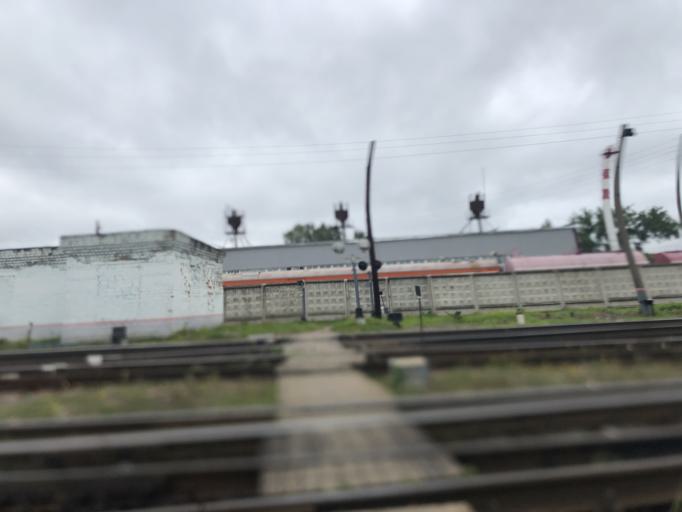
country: RU
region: Tverskaya
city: Rzhev
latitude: 56.2392
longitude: 34.3355
